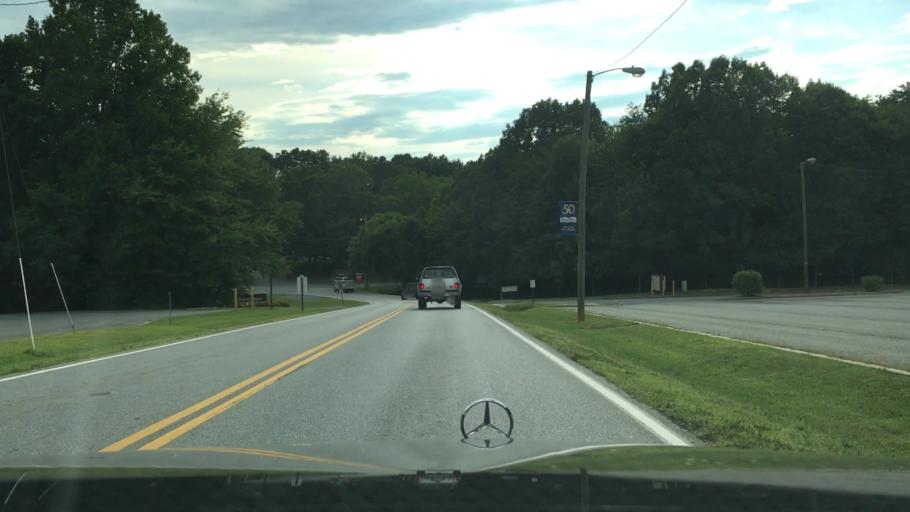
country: US
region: Virginia
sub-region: City of Lynchburg
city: West Lynchburg
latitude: 37.3564
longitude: -79.1871
